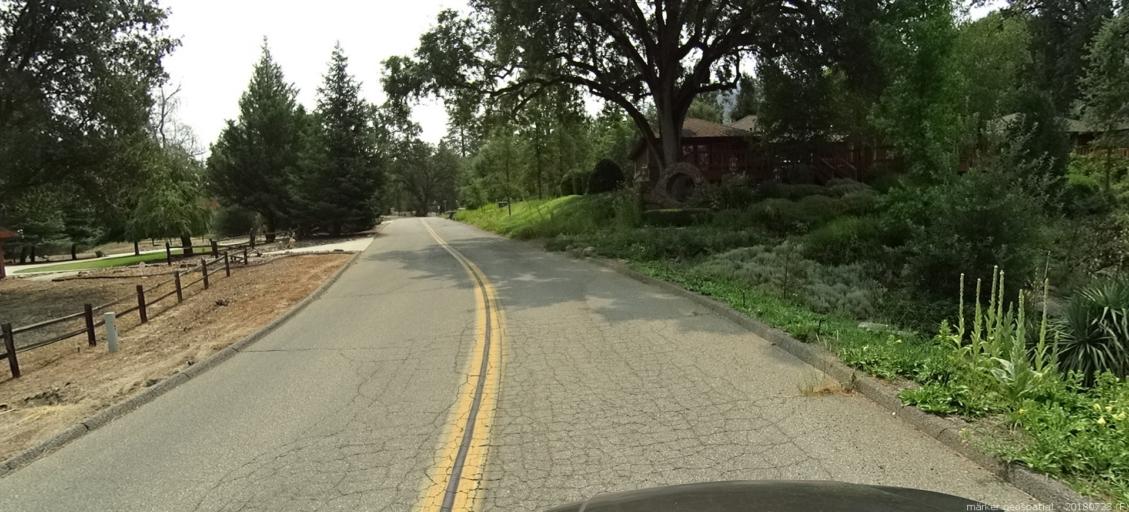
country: US
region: California
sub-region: Madera County
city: Ahwahnee
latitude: 37.3347
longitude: -119.7069
